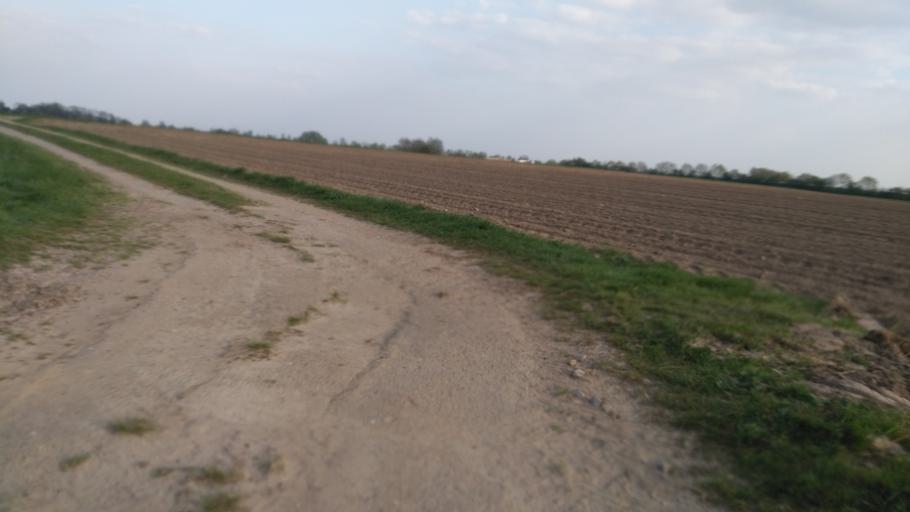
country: DE
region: Lower Saxony
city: Apensen
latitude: 53.4623
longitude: 9.6427
